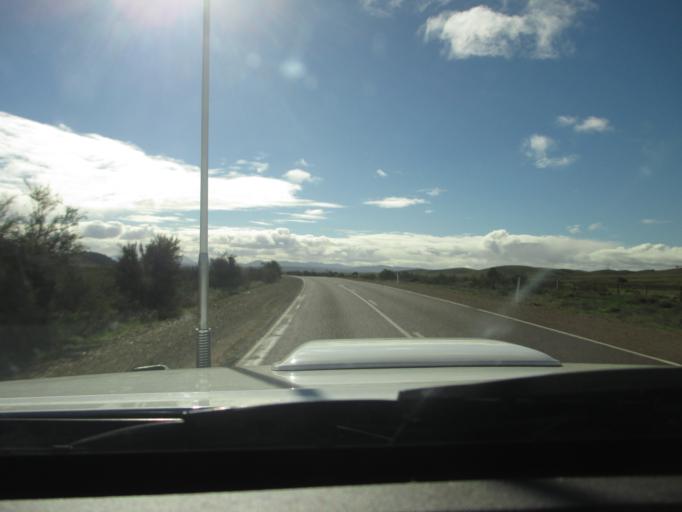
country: AU
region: South Australia
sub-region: Flinders Ranges
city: Quorn
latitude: -31.9283
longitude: 138.4194
